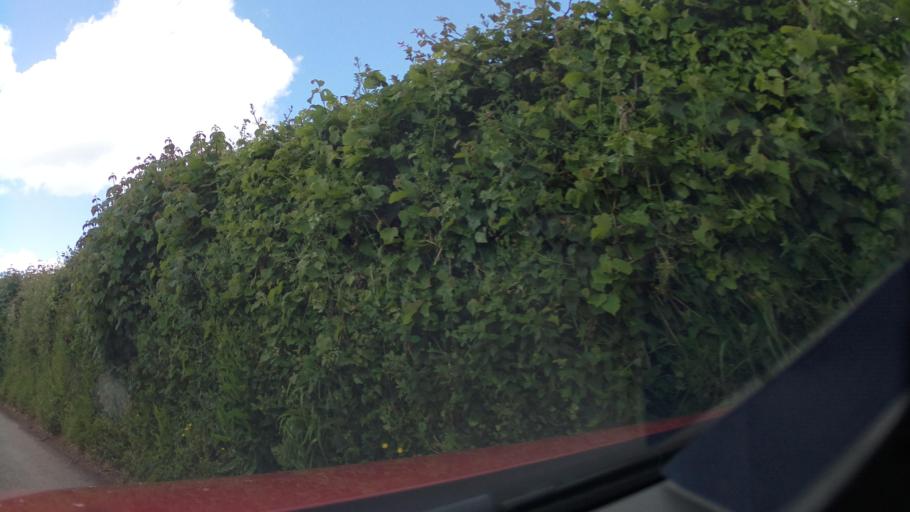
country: GB
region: England
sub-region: Devon
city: Dartmouth
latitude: 50.3560
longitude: -3.5413
